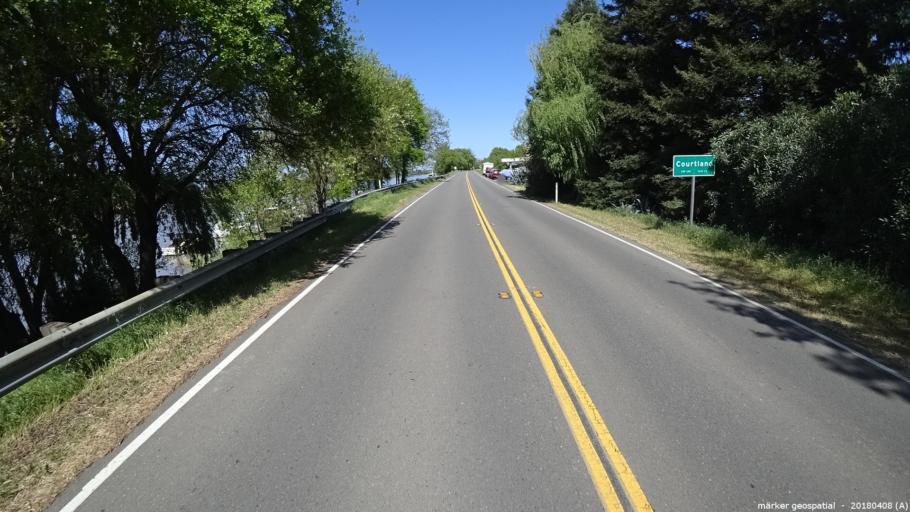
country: US
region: California
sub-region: Sacramento County
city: Walnut Grove
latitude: 38.3277
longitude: -121.5735
